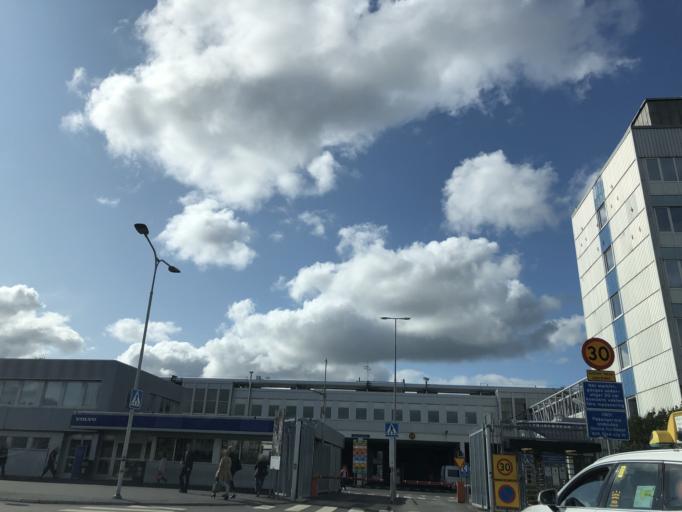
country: SE
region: Vaestra Goetaland
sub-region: Goteborg
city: Torslanda
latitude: 57.7188
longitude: 11.8413
